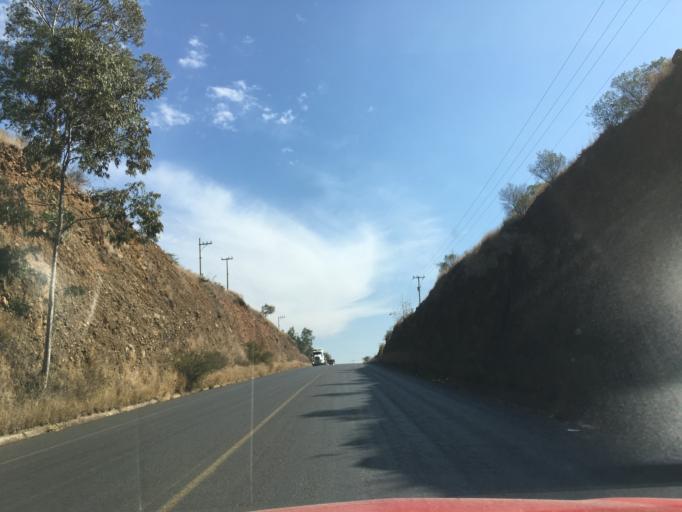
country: MX
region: Michoacan
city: Ciudad Hidalgo
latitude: 19.7075
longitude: -100.5527
